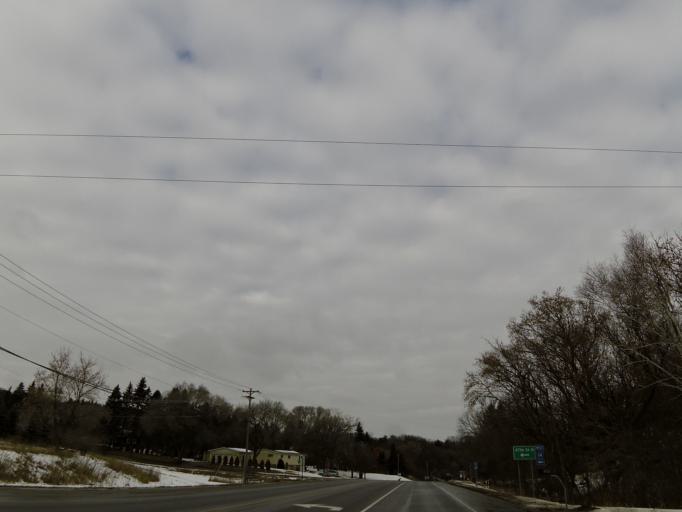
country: US
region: Minnesota
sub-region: Washington County
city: Oak Park Heights
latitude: 45.0170
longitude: -92.7973
